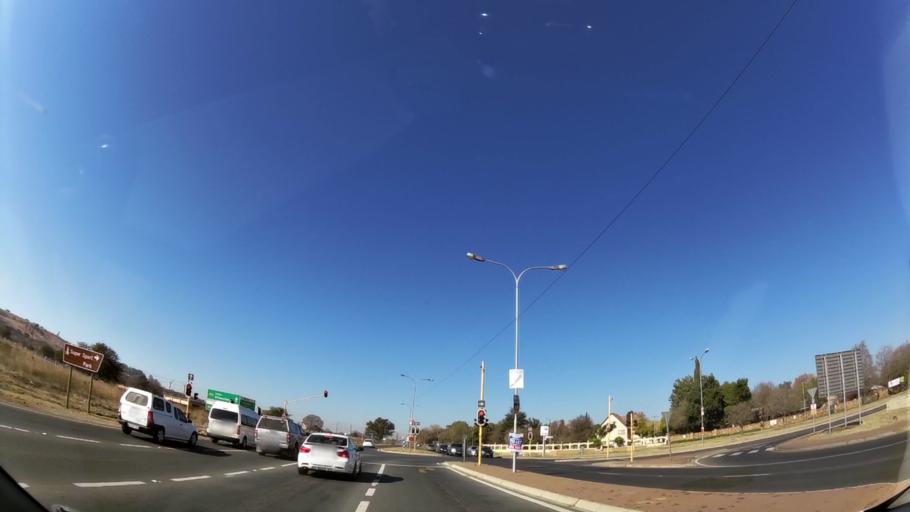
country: ZA
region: Gauteng
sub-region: City of Tshwane Metropolitan Municipality
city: Centurion
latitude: -25.8616
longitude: 28.2212
